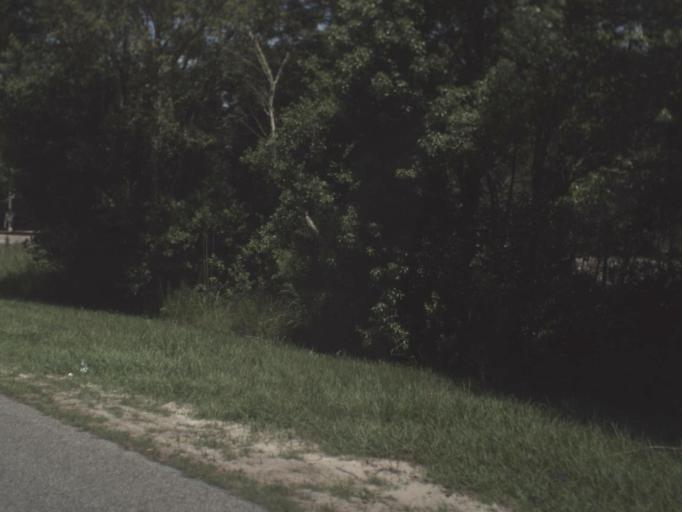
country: US
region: Florida
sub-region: Suwannee County
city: Live Oak
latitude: 30.3273
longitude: -83.0542
